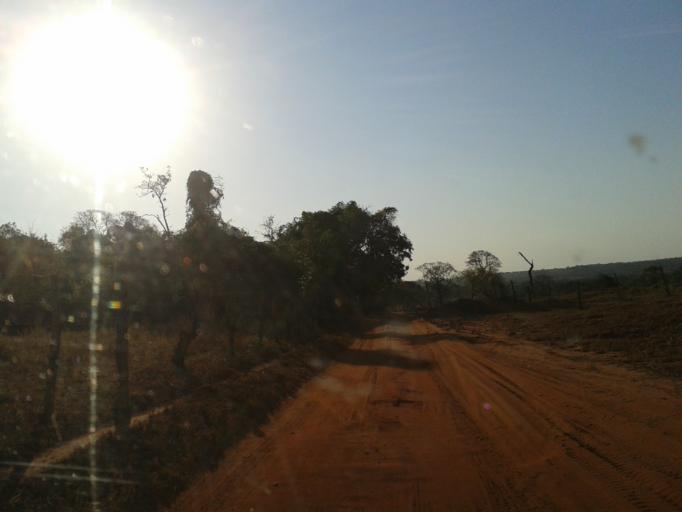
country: BR
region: Minas Gerais
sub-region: Ituiutaba
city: Ituiutaba
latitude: -19.2443
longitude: -49.5909
